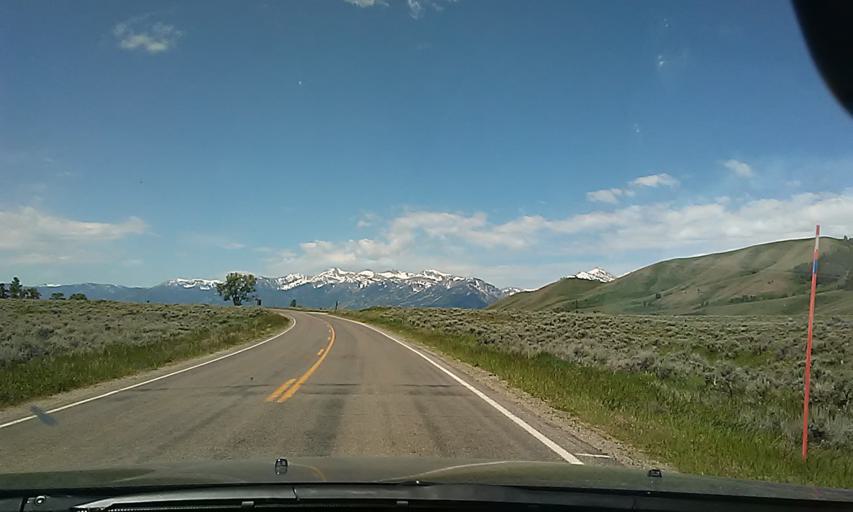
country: US
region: Wyoming
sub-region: Teton County
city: Jackson
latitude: 43.6252
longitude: -110.6625
